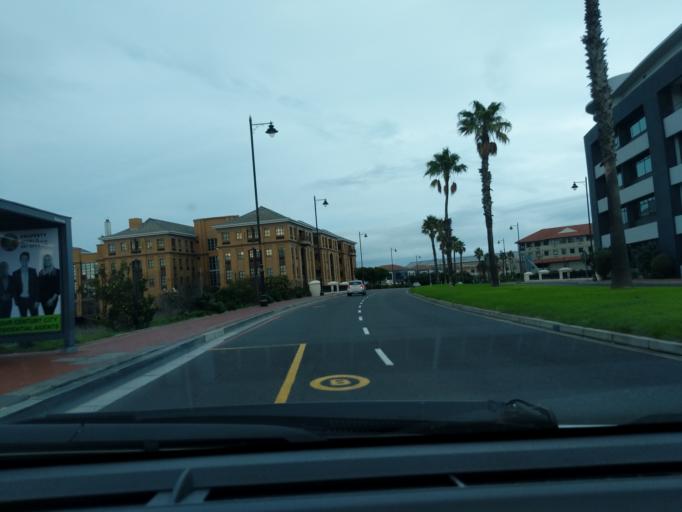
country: ZA
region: Western Cape
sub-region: City of Cape Town
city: Sunset Beach
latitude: -33.8868
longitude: 18.5203
